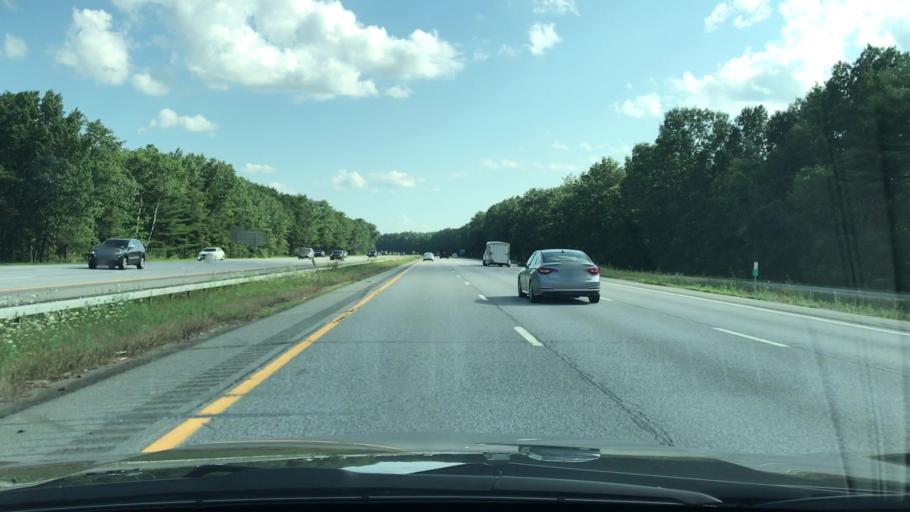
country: US
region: New York
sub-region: Warren County
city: West Glens Falls
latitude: 43.2962
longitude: -73.6796
